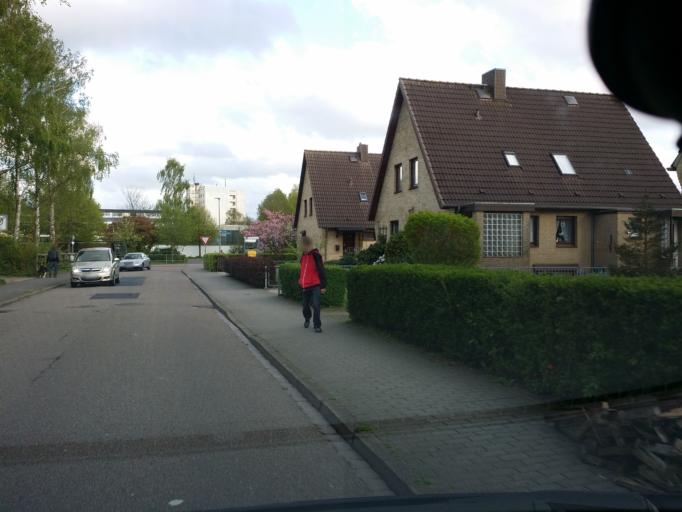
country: DE
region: Schleswig-Holstein
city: Rendsburg
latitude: 54.3210
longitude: 9.6409
